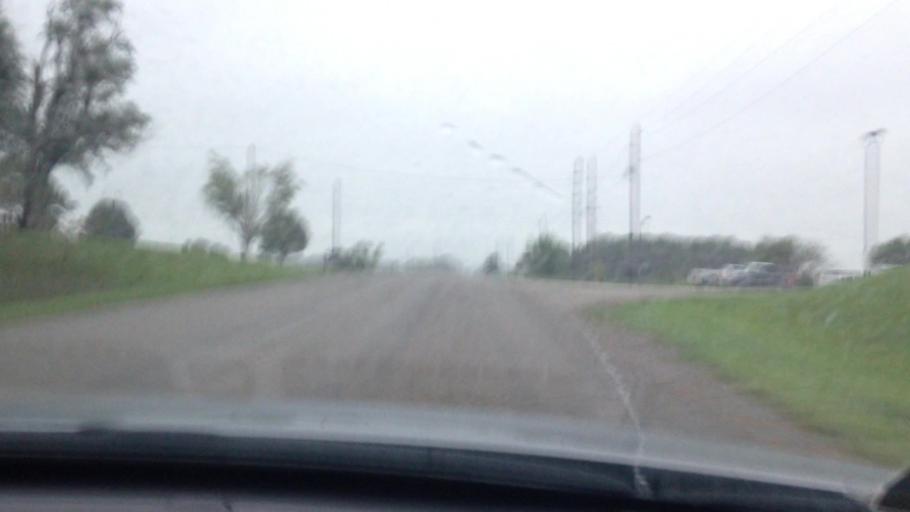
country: US
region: Kansas
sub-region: Brown County
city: Hiawatha
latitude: 39.8453
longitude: -95.5459
